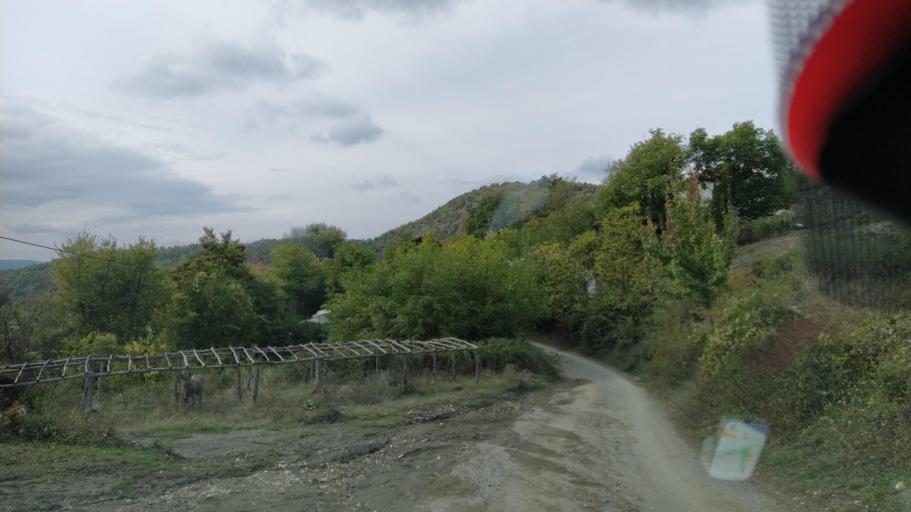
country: MK
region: Strumica
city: Veljusa
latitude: 41.5118
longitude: 22.4930
